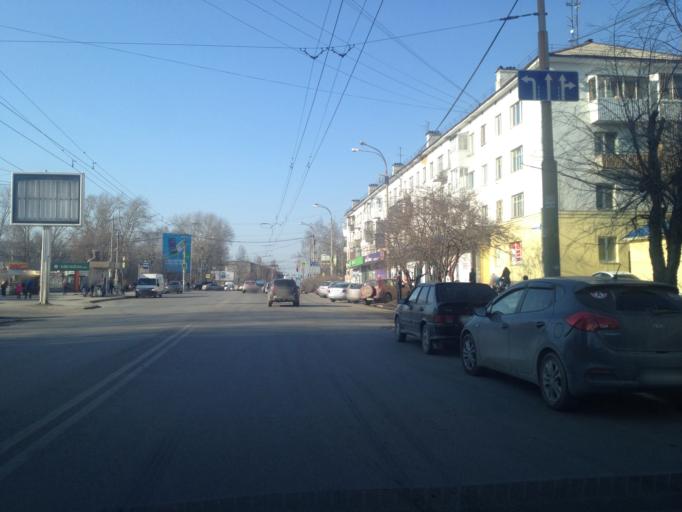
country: RU
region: Sverdlovsk
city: Yekaterinburg
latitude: 56.8561
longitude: 60.6542
